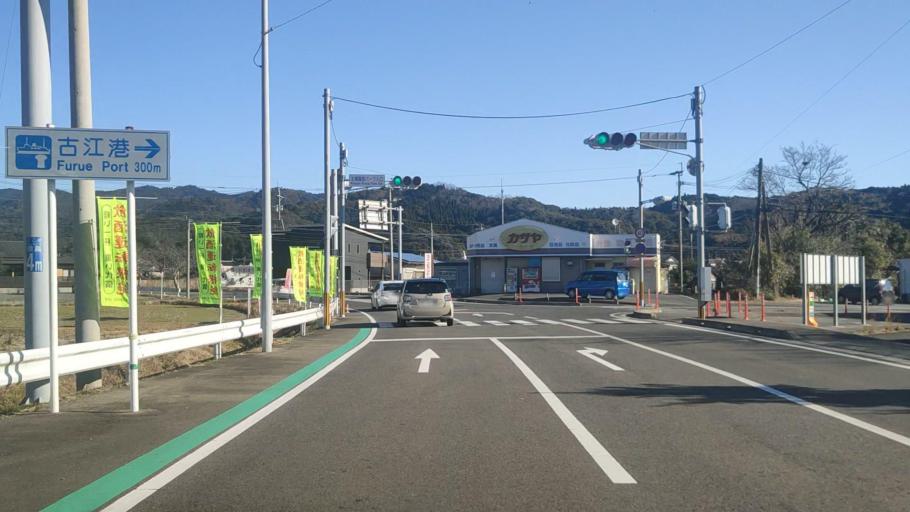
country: JP
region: Miyazaki
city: Nobeoka
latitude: 32.7066
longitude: 131.8184
